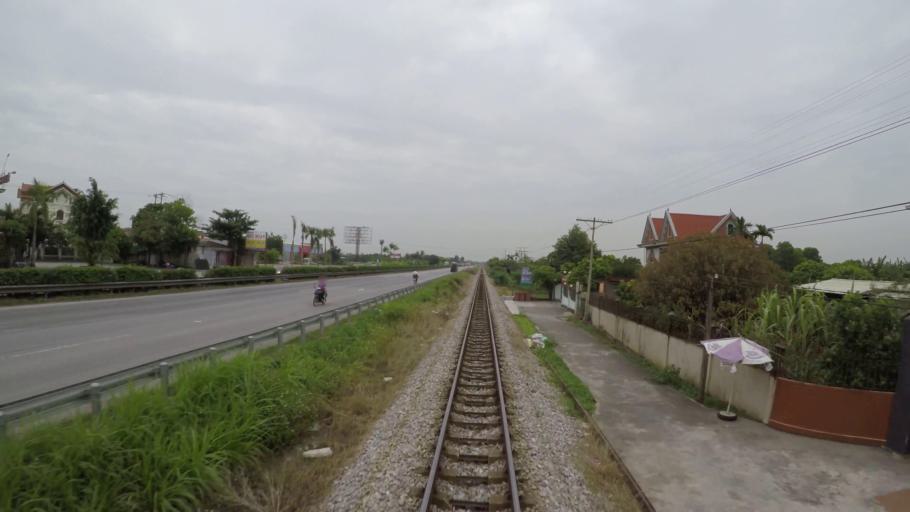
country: VN
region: Hai Duong
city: Phu Thai
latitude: 20.9711
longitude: 106.4429
